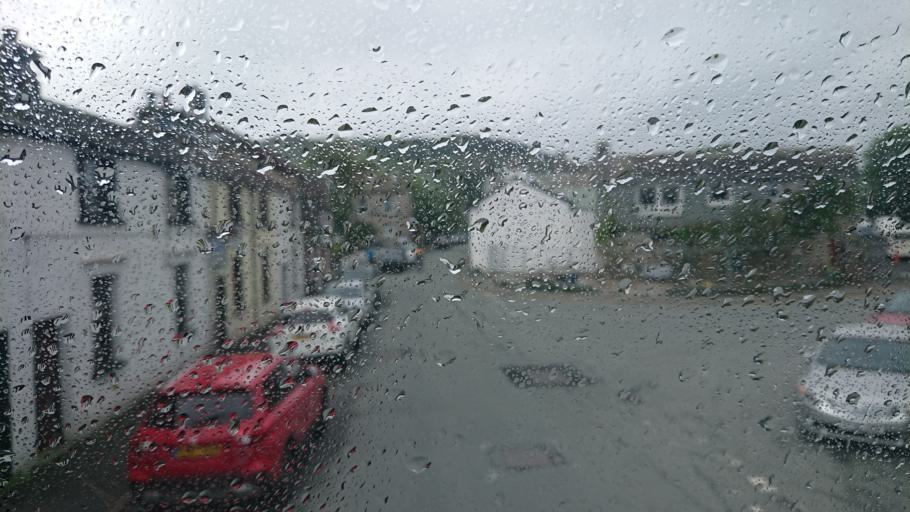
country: GB
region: England
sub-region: Cumbria
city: Kendal
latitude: 54.3766
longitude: -2.8157
